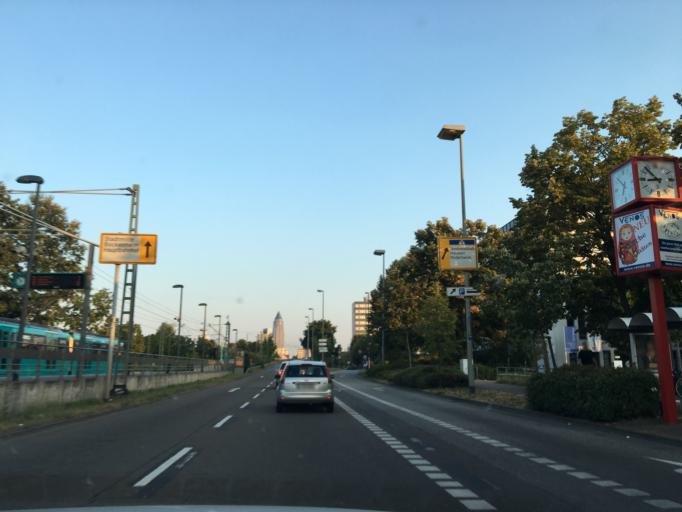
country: DE
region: Hesse
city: Niederrad
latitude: 50.1288
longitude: 8.6294
